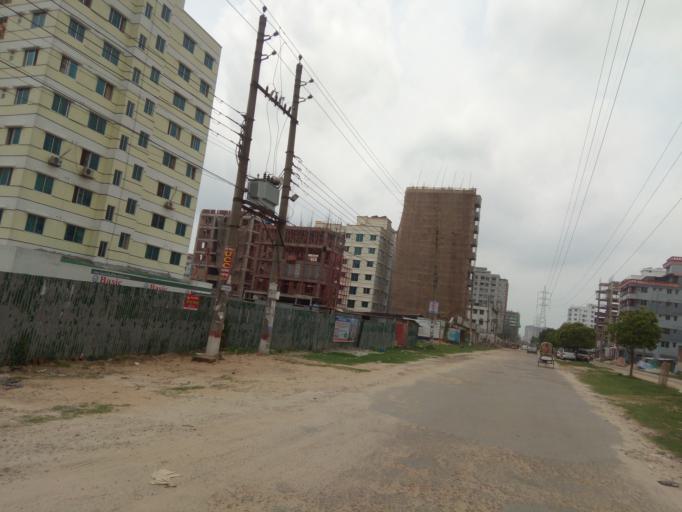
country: BD
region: Dhaka
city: Paltan
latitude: 23.7659
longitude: 90.4295
